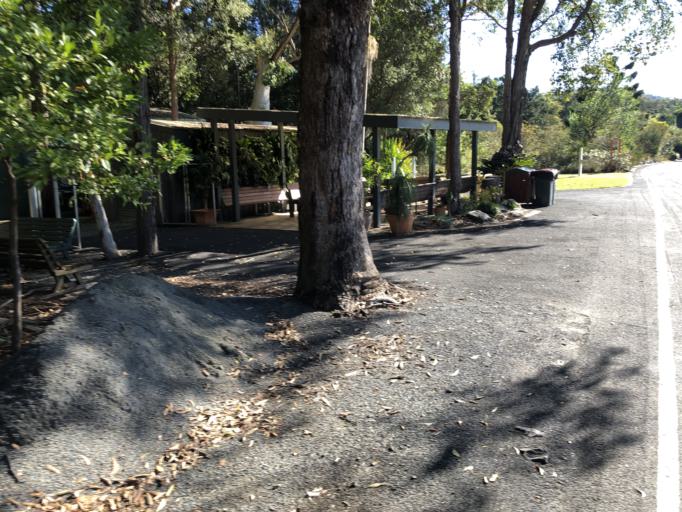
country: AU
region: New South Wales
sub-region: Coffs Harbour
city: Coffs Harbour
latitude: -30.2941
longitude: 153.1245
